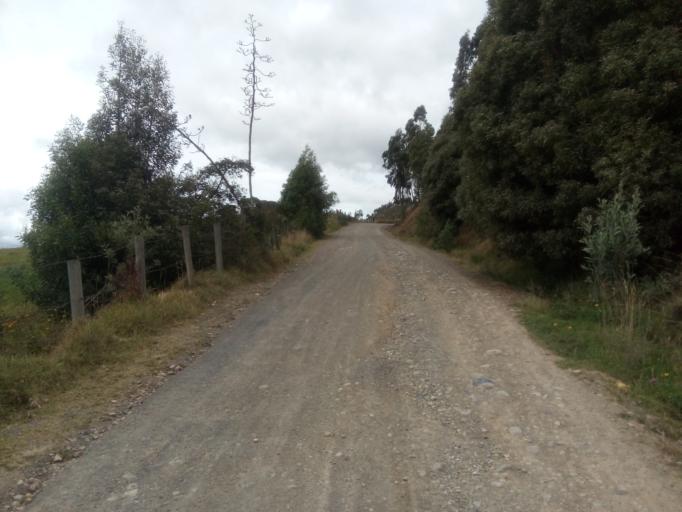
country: CO
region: Boyaca
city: Gameza
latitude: 5.8164
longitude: -72.8027
